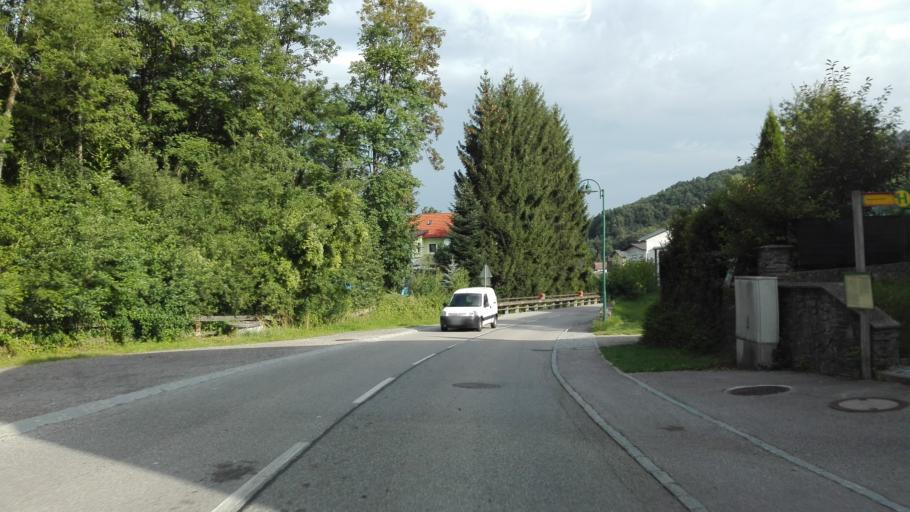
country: AT
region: Lower Austria
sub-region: Politischer Bezirk Sankt Polten
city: Stossing
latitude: 48.1232
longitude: 15.8131
